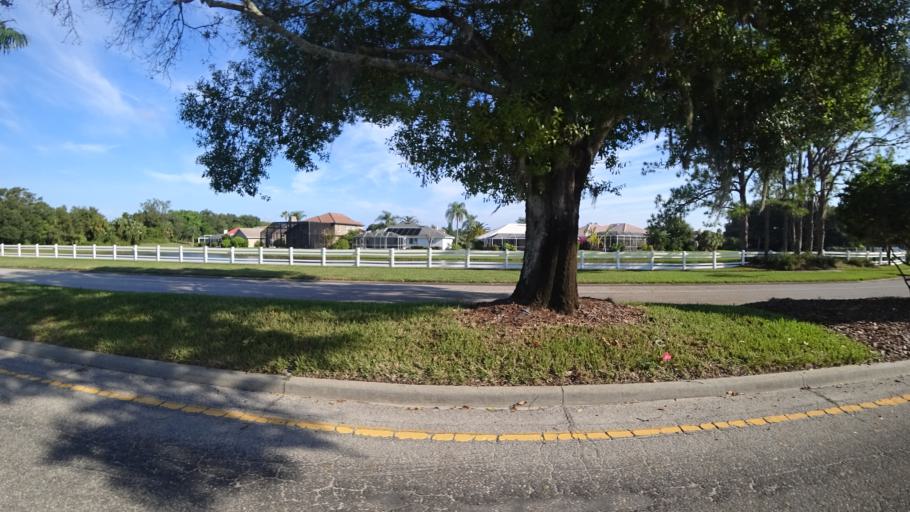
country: US
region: Florida
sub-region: Sarasota County
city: Desoto Lakes
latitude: 27.4149
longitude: -82.4884
